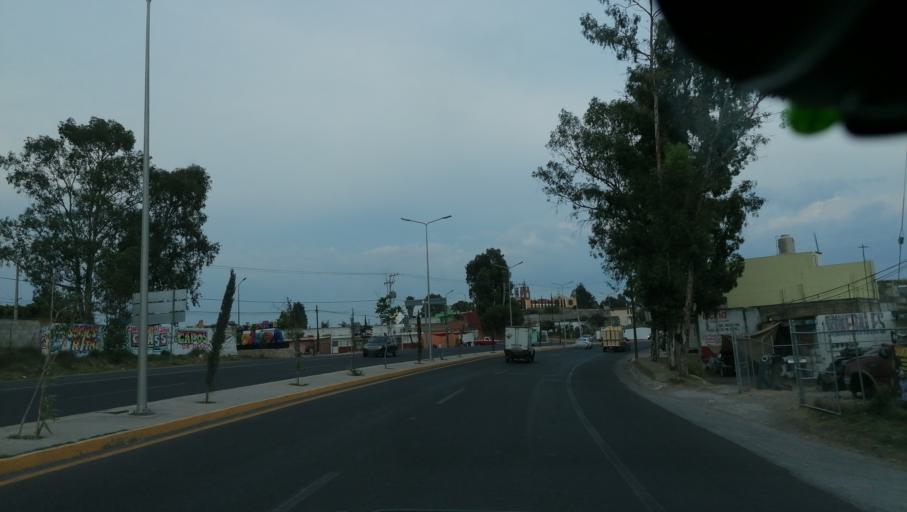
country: MX
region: Puebla
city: Tlazcalancingo
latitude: 19.0225
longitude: -98.3052
